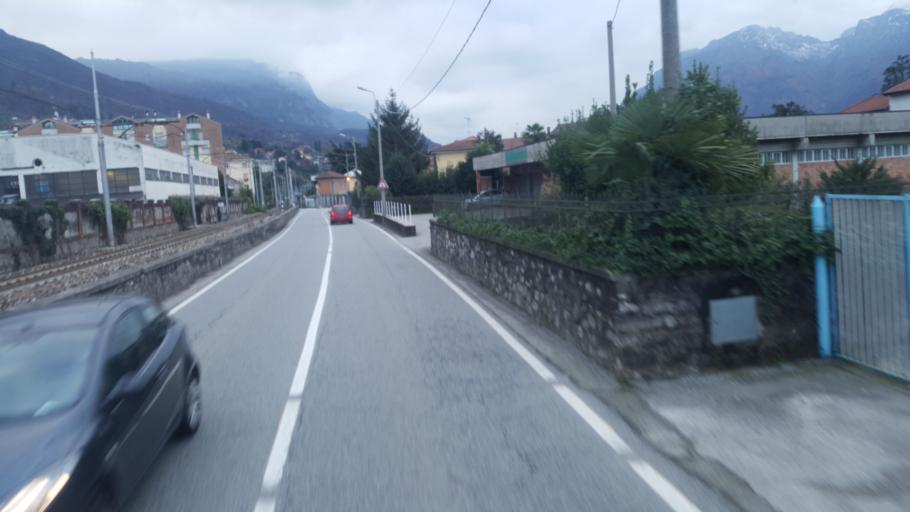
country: IT
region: Lombardy
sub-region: Provincia di Lecco
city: Mandello del Lario
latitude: 45.9180
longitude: 9.3168
